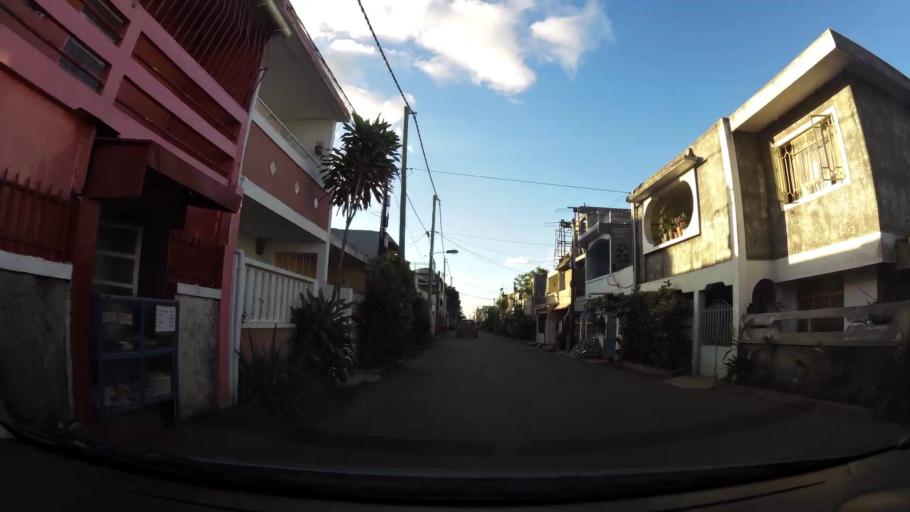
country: MU
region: Plaines Wilhems
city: Quatre Bornes
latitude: -20.2542
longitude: 57.4617
